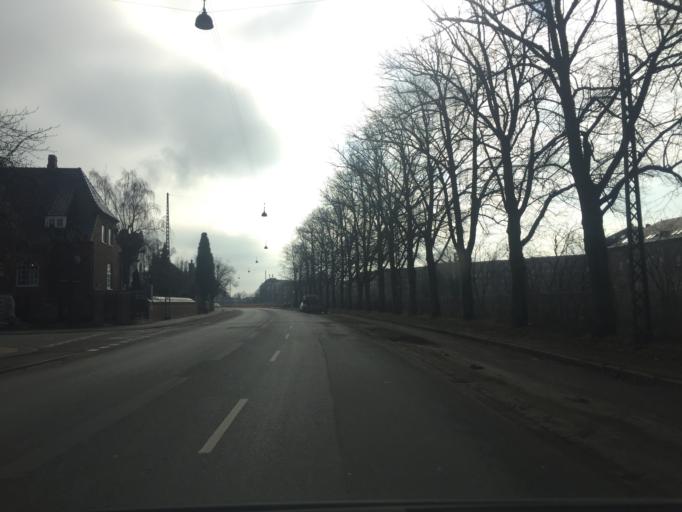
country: DK
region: Capital Region
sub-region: Gentofte Kommune
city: Charlottenlund
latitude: 55.7189
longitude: 12.5732
